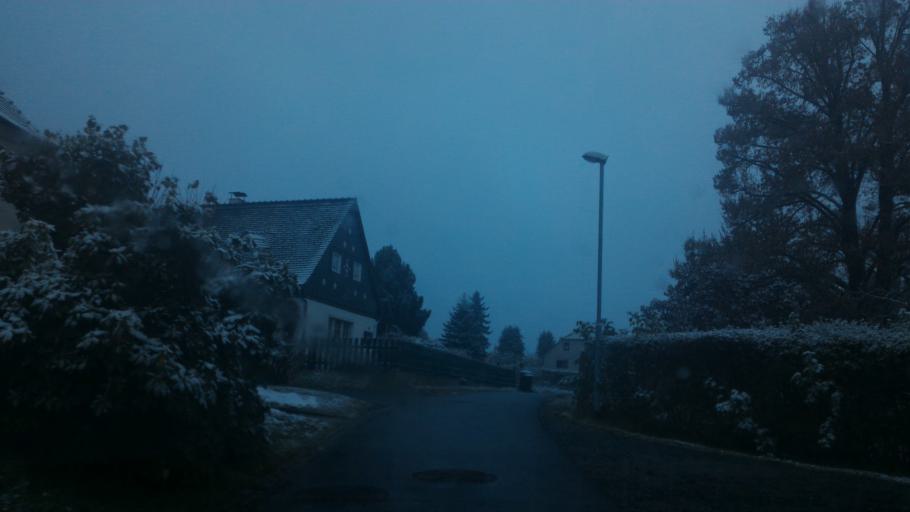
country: CZ
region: Ustecky
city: Jirikov
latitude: 51.0068
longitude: 14.5733
